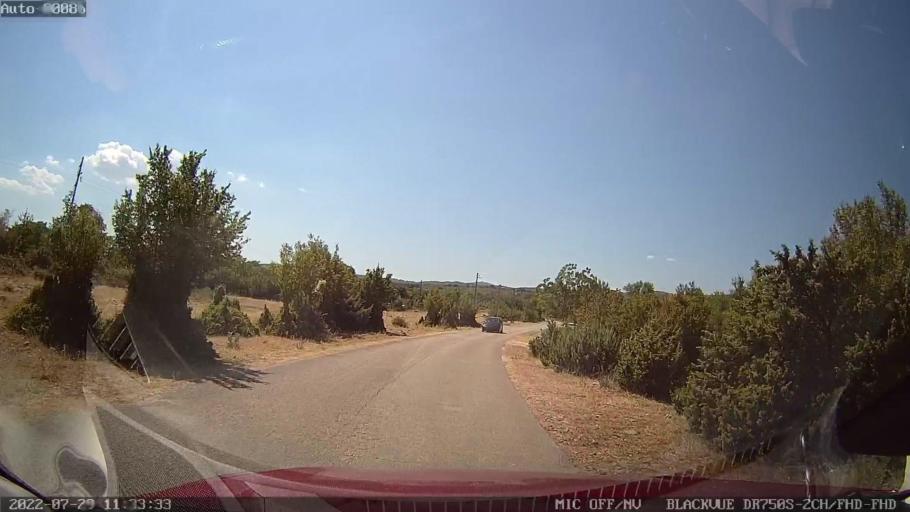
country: HR
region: Zadarska
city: Obrovac
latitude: 44.1849
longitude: 15.7325
